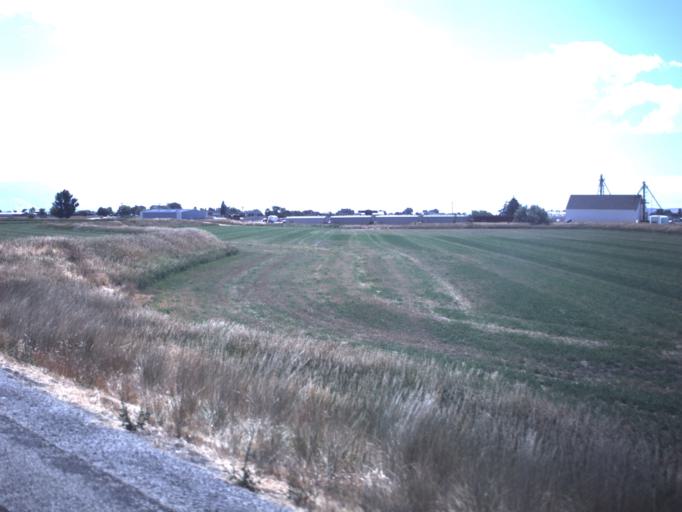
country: US
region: Utah
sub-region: Box Elder County
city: Garland
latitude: 41.7456
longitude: -112.1460
